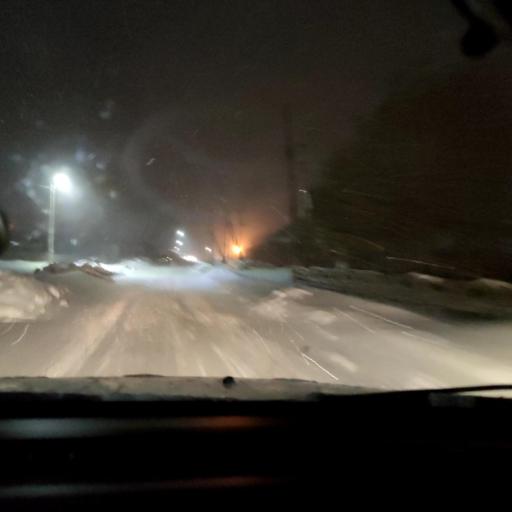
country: RU
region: Bashkortostan
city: Iglino
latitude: 54.8262
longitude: 56.3827
